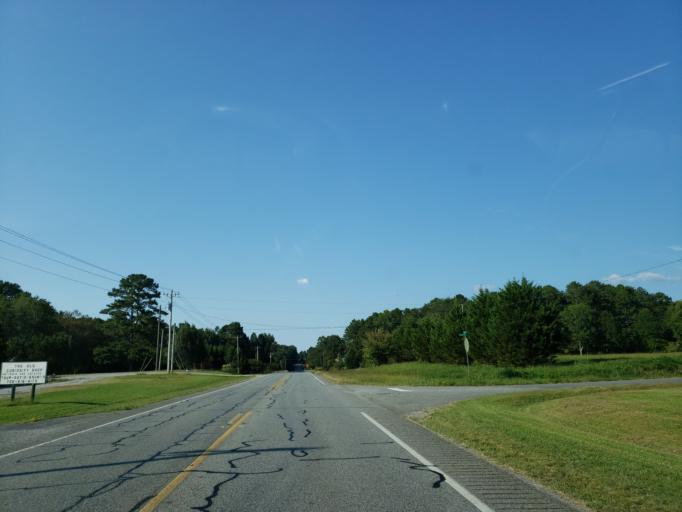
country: US
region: Tennessee
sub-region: Bradley County
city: Wildwood Lake
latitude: 34.9681
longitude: -84.7327
